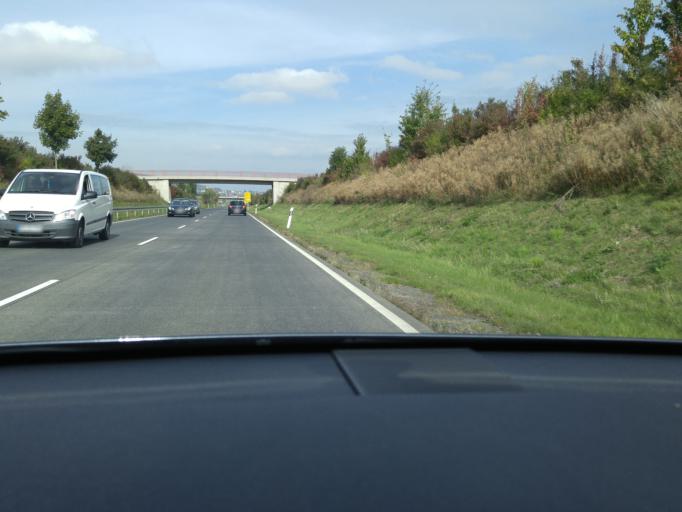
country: DE
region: Hesse
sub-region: Regierungsbezirk Darmstadt
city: Friedberg
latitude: 50.3265
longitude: 8.7352
